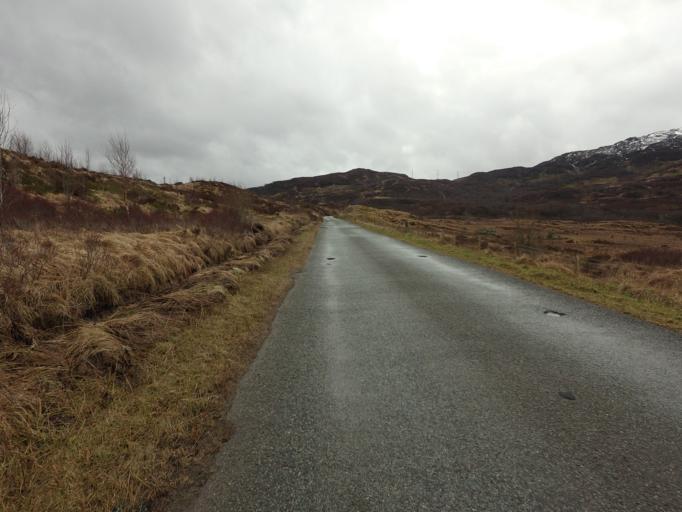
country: GB
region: Scotland
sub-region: West Dunbartonshire
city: Balloch
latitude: 56.2500
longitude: -4.5871
